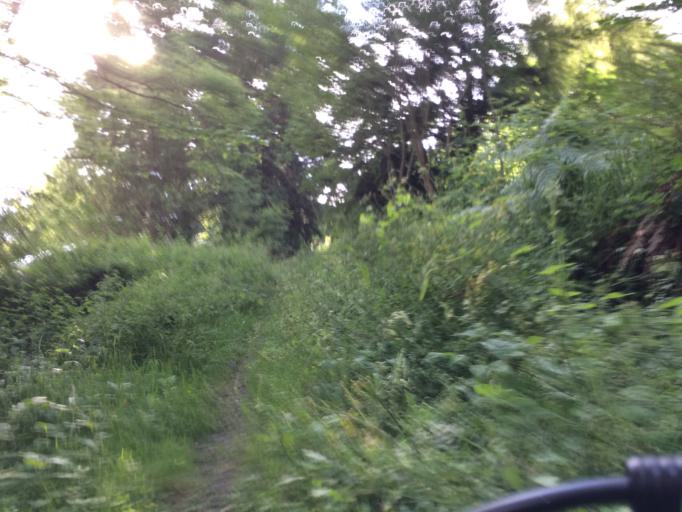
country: FR
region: Brittany
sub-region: Departement du Finistere
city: Logonna-Daoulas
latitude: 48.3227
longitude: -4.2861
